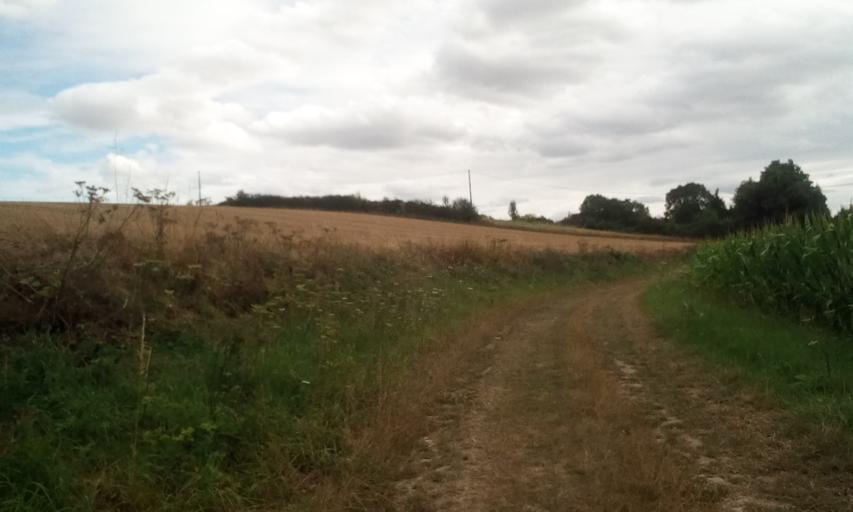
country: FR
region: Lower Normandy
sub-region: Departement du Calvados
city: Bellengreville
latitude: 49.1093
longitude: -0.1969
